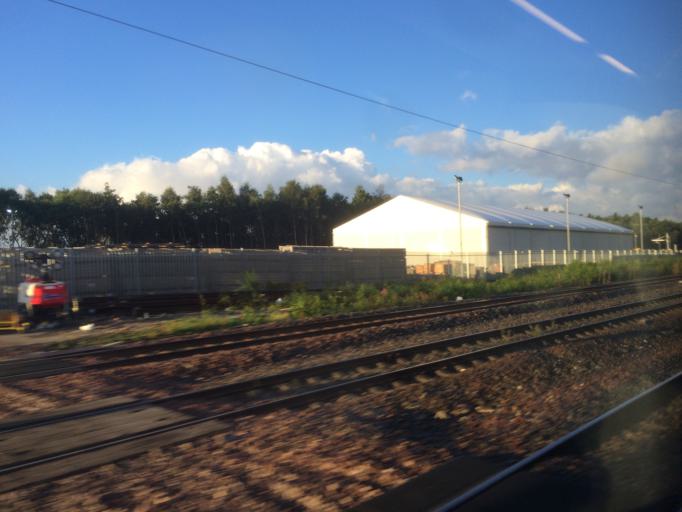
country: GB
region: Scotland
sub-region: East Dunbartonshire
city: Kirkintilloch
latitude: 55.9155
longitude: -4.1787
